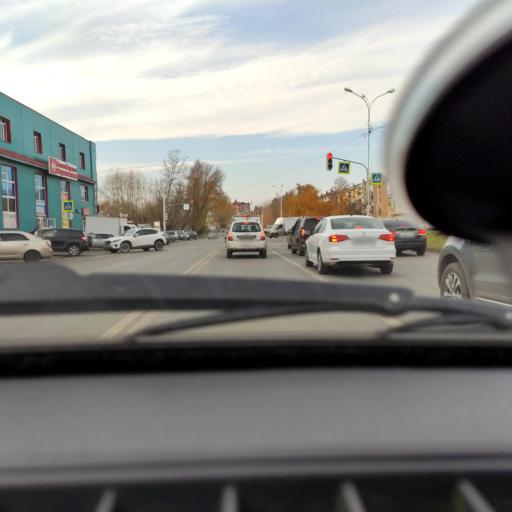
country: RU
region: Bashkortostan
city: Ufa
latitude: 54.8074
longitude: 56.0990
